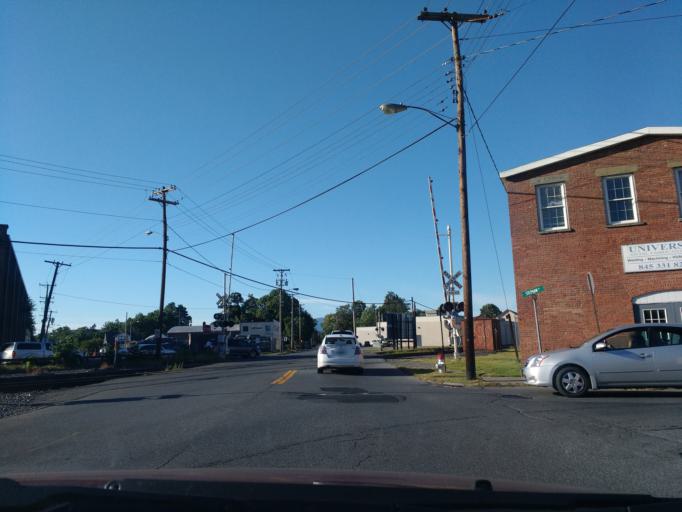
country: US
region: New York
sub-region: Ulster County
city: Kingston
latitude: 41.9345
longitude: -73.9975
